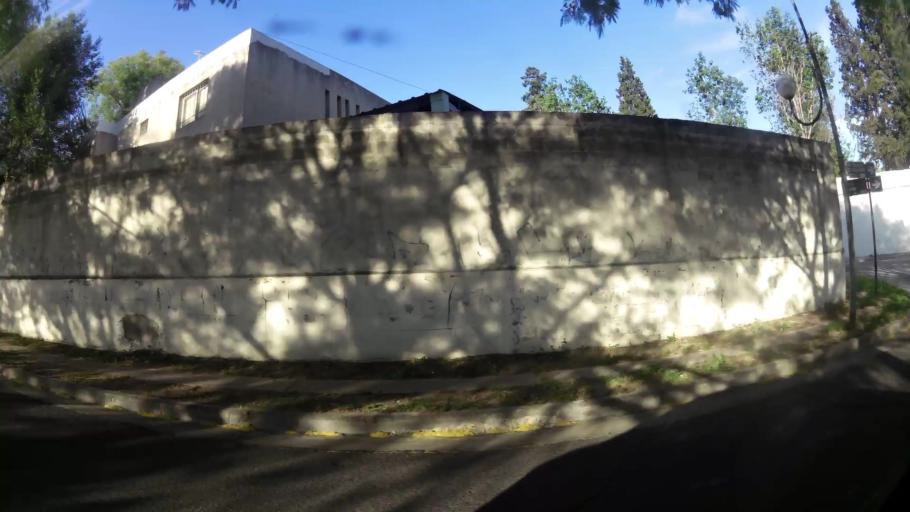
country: AR
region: Cordoba
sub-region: Departamento de Capital
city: Cordoba
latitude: -31.3897
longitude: -64.2346
